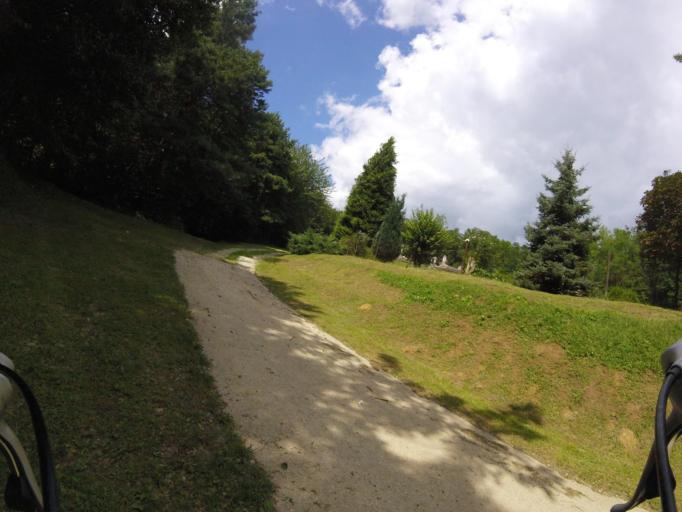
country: HU
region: Zala
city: Becsehely
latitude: 46.5026
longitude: 16.8074
